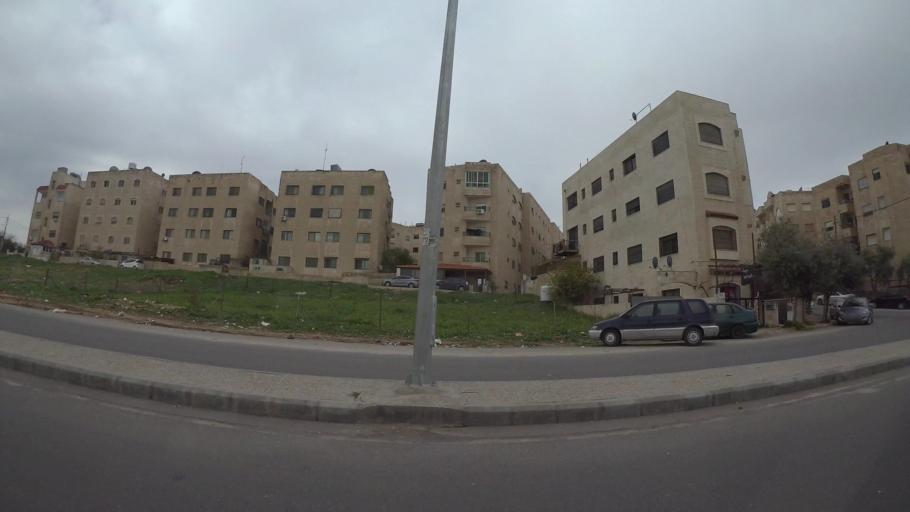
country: JO
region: Amman
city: Amman
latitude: 31.9824
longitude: 35.9310
